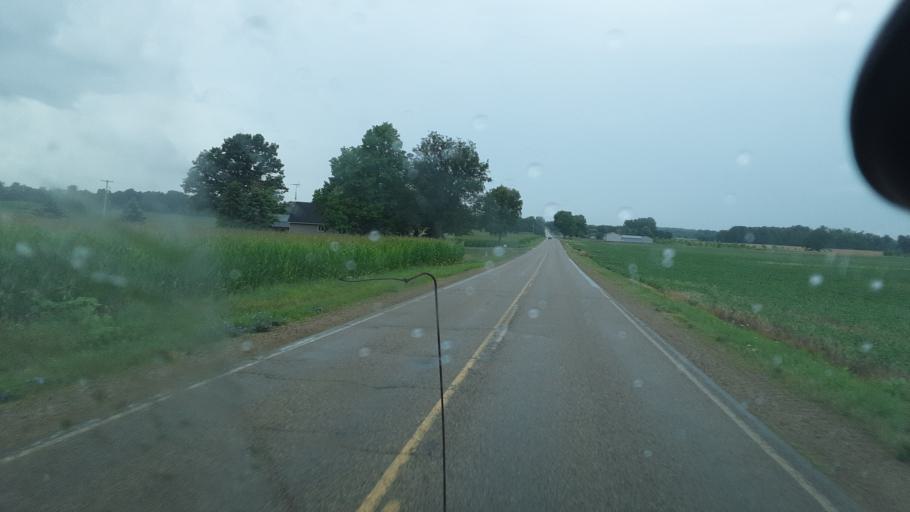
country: US
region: Michigan
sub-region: Hillsdale County
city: Reading
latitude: 41.7081
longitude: -84.7383
